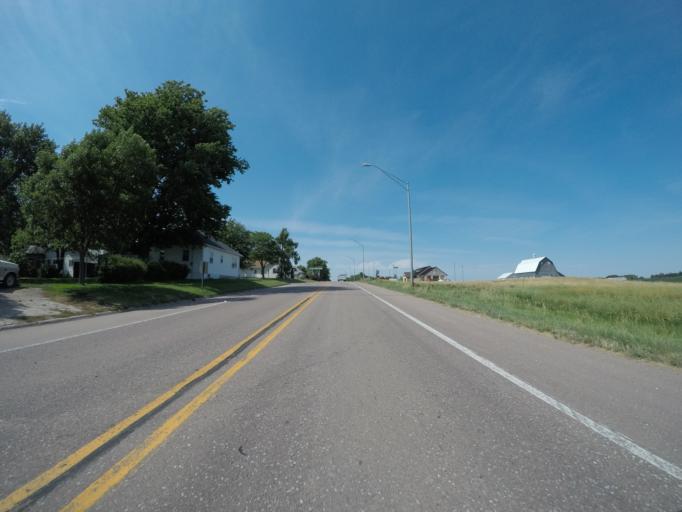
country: US
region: Nebraska
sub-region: Webster County
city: Red Cloud
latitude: 40.3310
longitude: -98.4439
